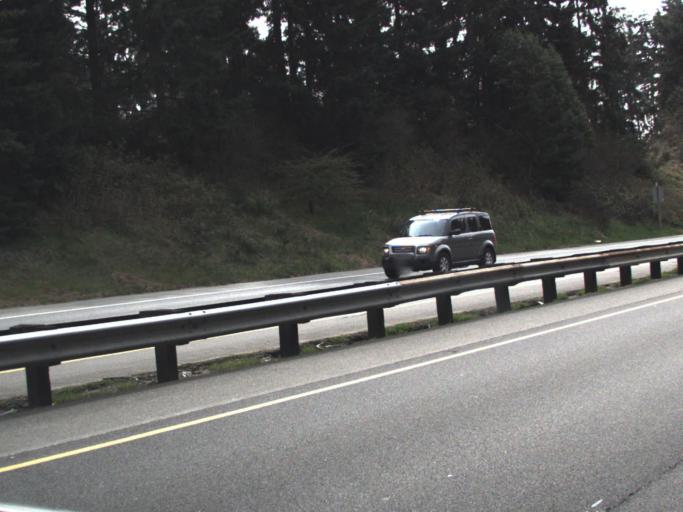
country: US
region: Washington
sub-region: King County
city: Boulevard Park
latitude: 47.4939
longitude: -122.3251
